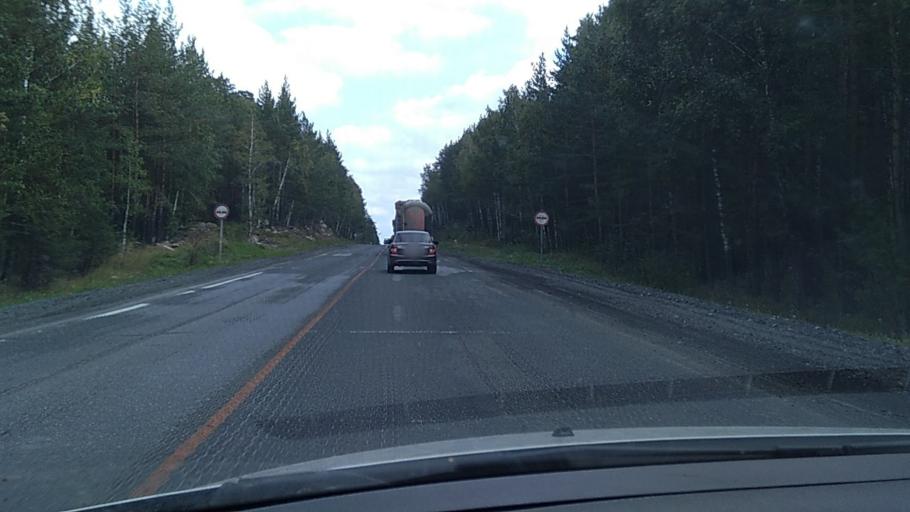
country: RU
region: Chelyabinsk
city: Miass
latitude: 54.9305
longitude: 60.1719
